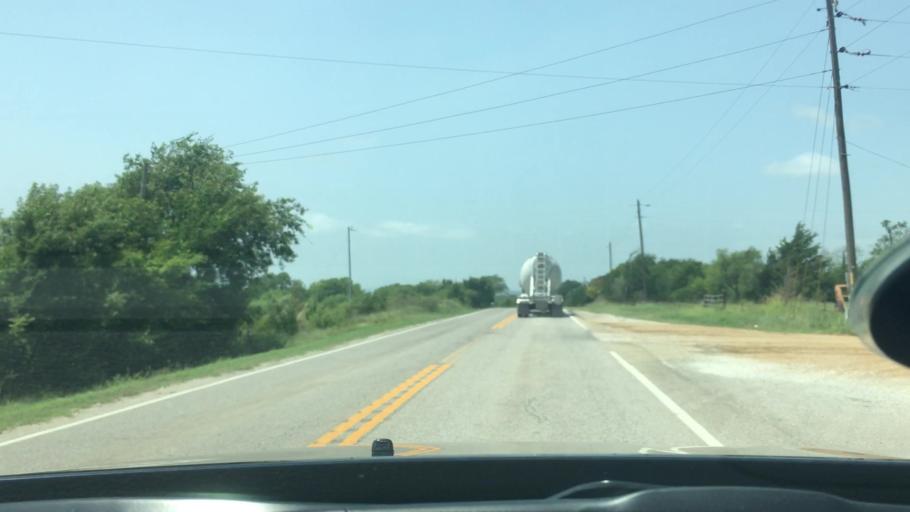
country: US
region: Oklahoma
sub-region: Murray County
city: Sulphur
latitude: 34.5109
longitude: -96.9322
